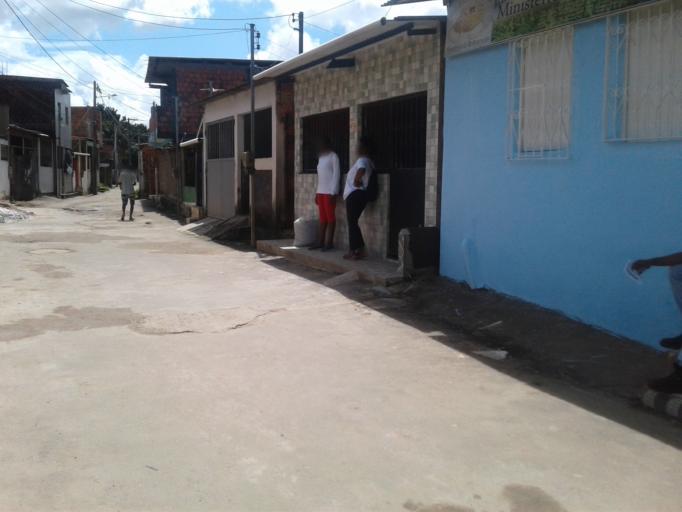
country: BR
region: Bahia
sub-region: Salvador
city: Salvador
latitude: -12.9096
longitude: -38.4710
